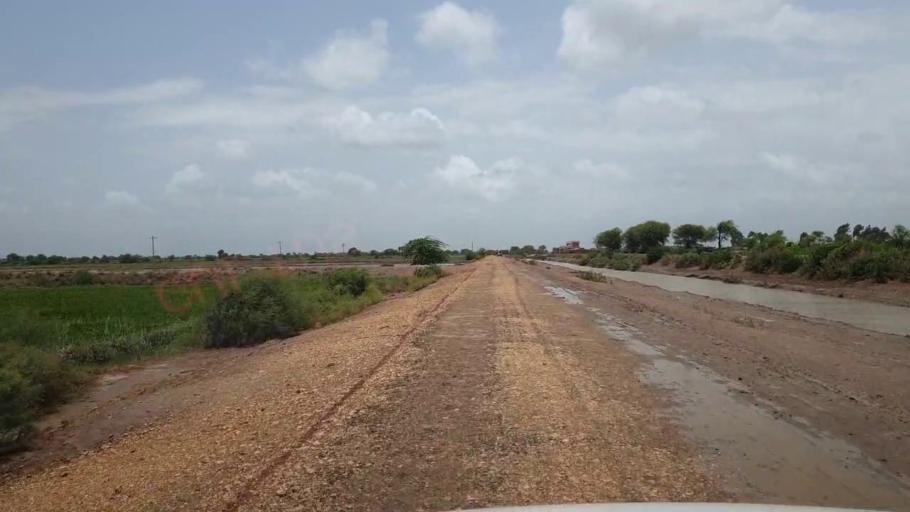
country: PK
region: Sindh
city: Kario
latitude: 24.7147
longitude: 68.5876
